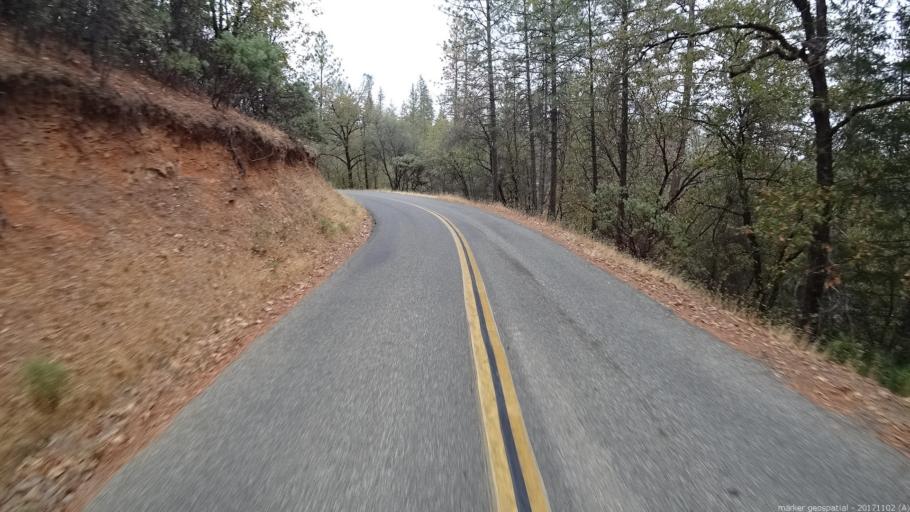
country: US
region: California
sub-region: Shasta County
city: Bella Vista
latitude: 40.7435
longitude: -122.2403
